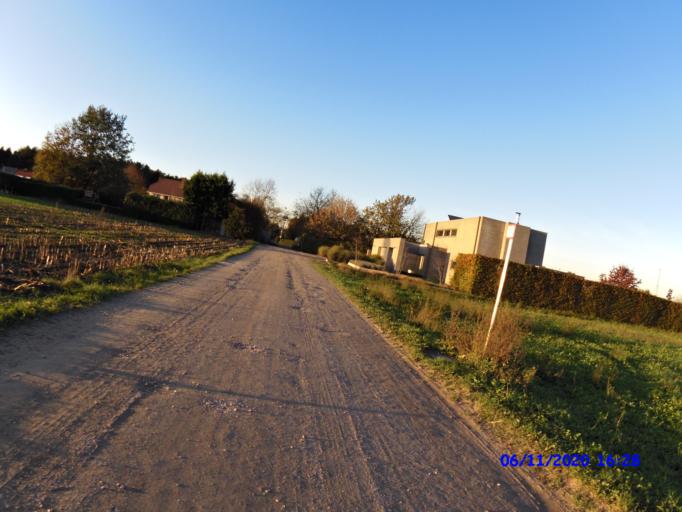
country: BE
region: Flanders
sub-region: Provincie Antwerpen
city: Mol
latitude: 51.1848
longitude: 5.0633
